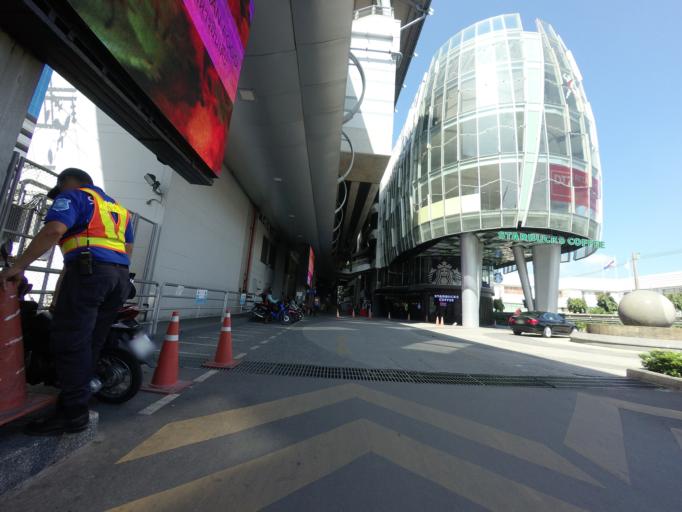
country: TH
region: Bangkok
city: Watthana
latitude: 13.7429
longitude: 100.6013
